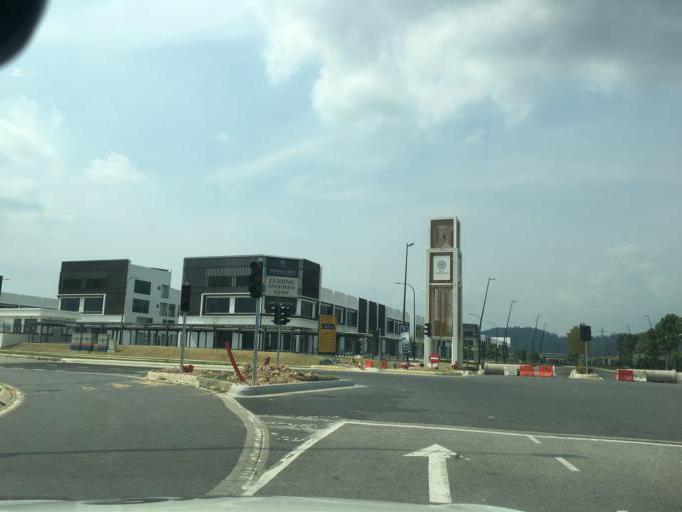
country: MY
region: Selangor
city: Shah Alam
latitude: 3.0853
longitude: 101.4764
